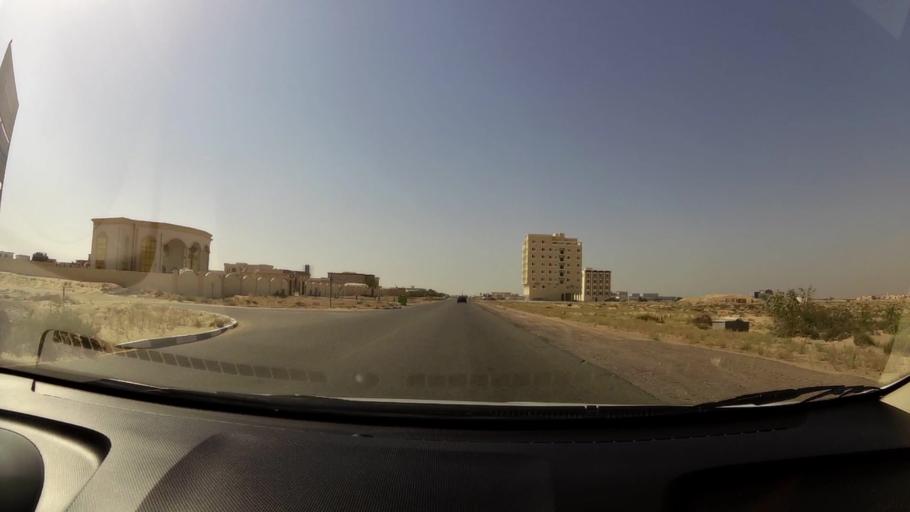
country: AE
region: Umm al Qaywayn
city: Umm al Qaywayn
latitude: 25.4937
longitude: 55.5991
